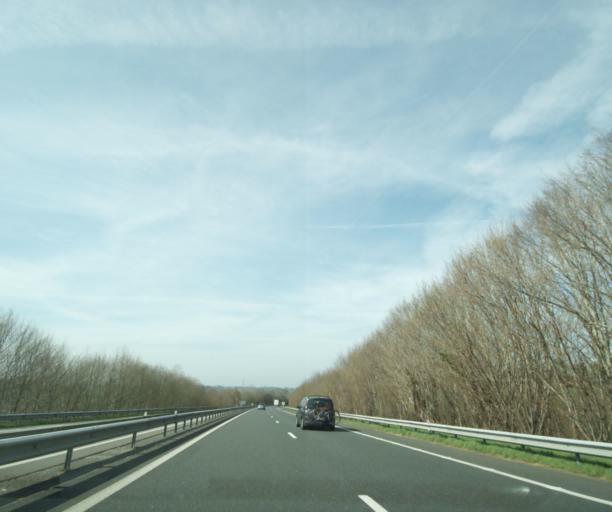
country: FR
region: Limousin
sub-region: Departement de la Correze
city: Uzerche
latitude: 45.4069
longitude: 1.5461
